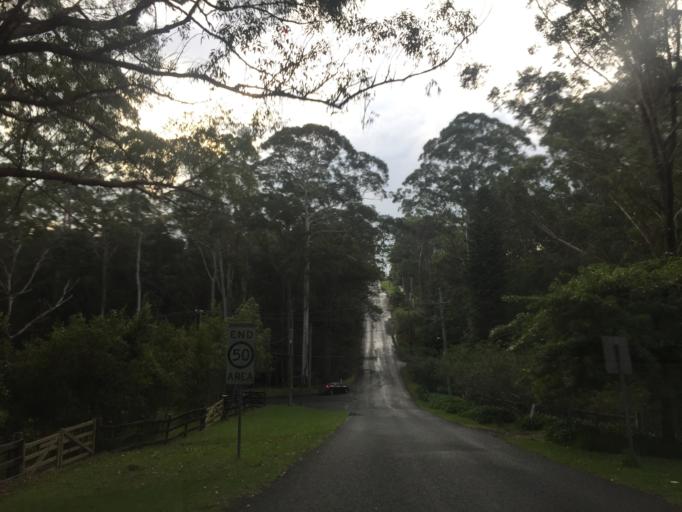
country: AU
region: New South Wales
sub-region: The Hills Shire
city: Glenhaven
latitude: -33.6841
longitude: 151.0217
